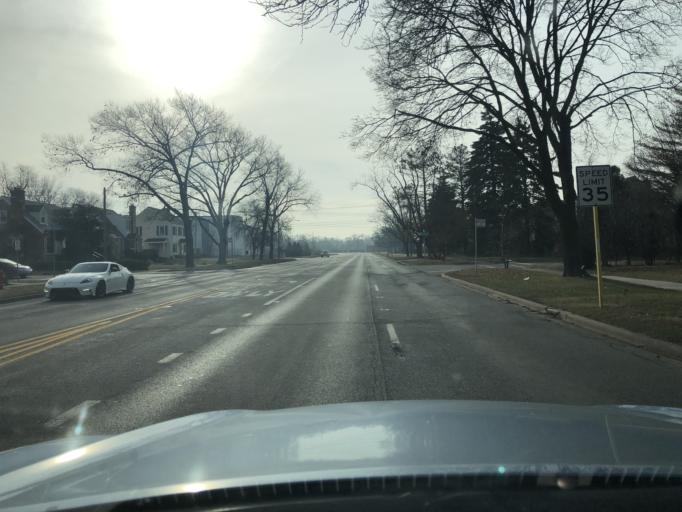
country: US
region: Illinois
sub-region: Cook County
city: Des Plaines
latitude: 42.0461
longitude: -87.9121
